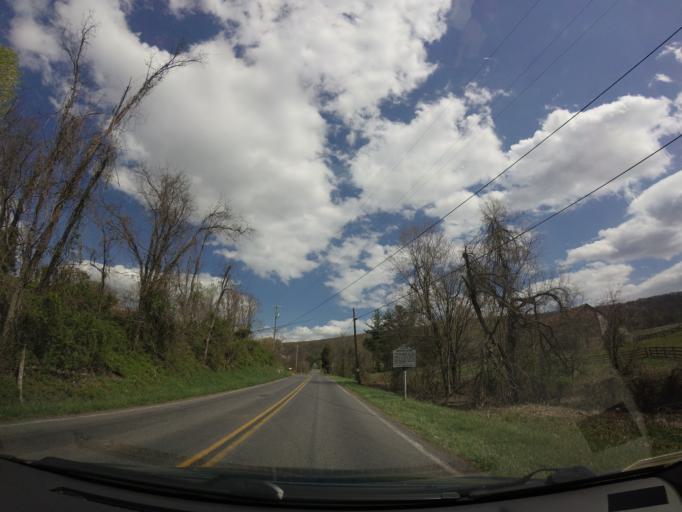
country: US
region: Maryland
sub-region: Frederick County
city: Brunswick
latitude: 39.3998
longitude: -77.6544
